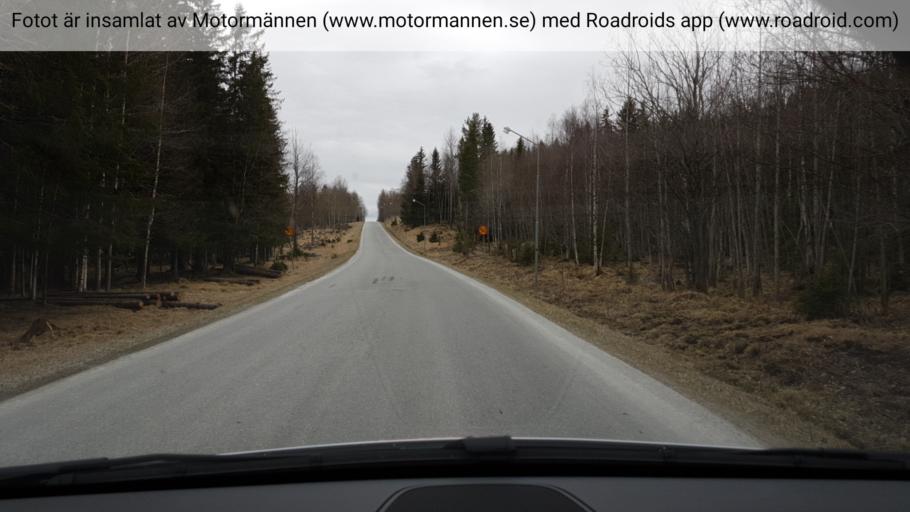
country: SE
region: Jaemtland
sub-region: Bergs Kommun
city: Hoverberg
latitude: 62.9124
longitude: 14.3149
